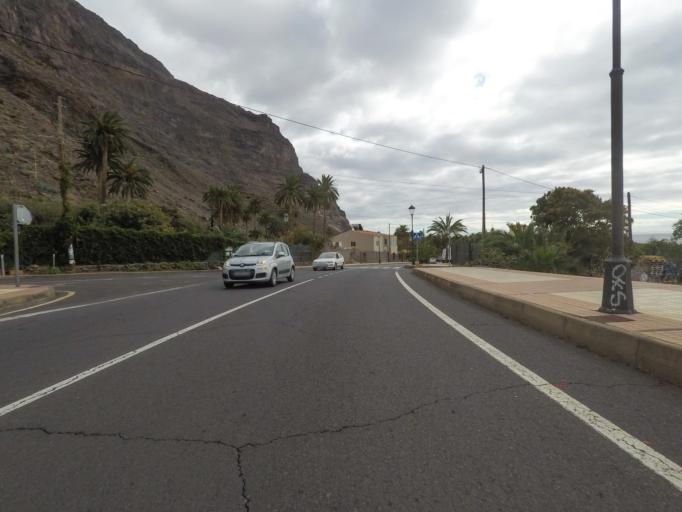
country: ES
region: Canary Islands
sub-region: Provincia de Santa Cruz de Tenerife
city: Alajero
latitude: 28.0935
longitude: -17.3354
